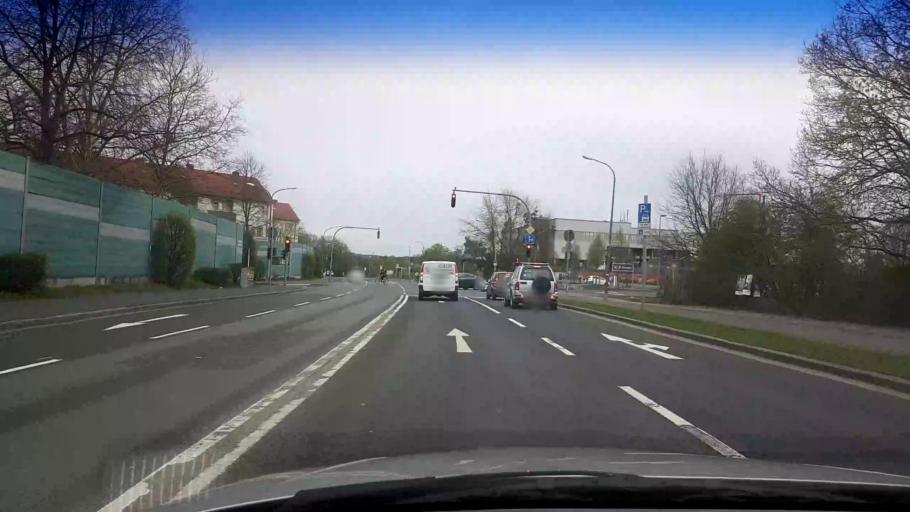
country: DE
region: Bavaria
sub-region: Upper Franconia
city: Bamberg
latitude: 49.8807
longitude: 10.9175
